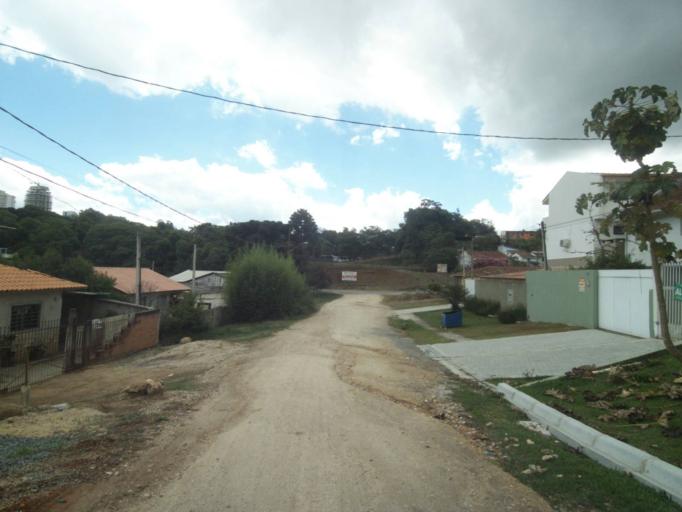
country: BR
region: Parana
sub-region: Curitiba
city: Curitiba
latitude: -25.4339
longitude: -49.3303
